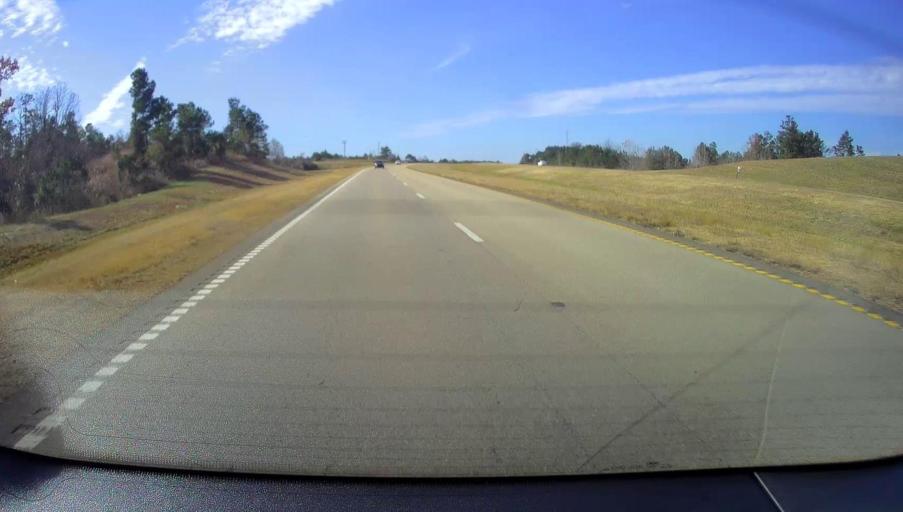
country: US
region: Mississippi
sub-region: Benton County
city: Ashland
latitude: 34.9533
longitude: -89.0024
